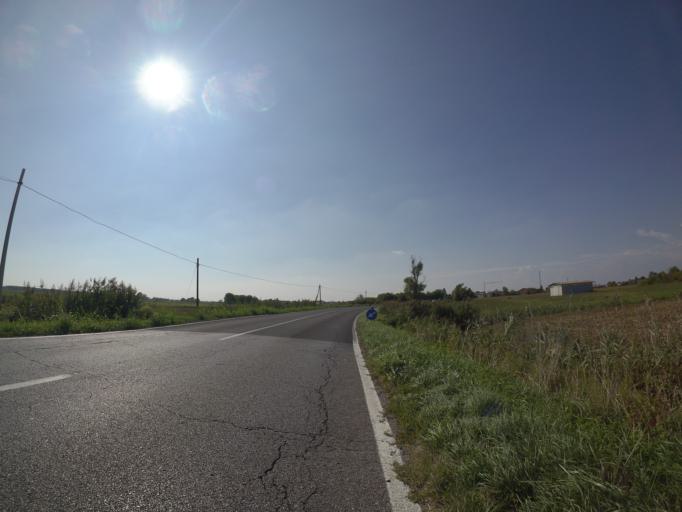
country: IT
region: Friuli Venezia Giulia
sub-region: Provincia di Udine
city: Muzzana del Turgnano
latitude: 45.8149
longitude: 13.1392
